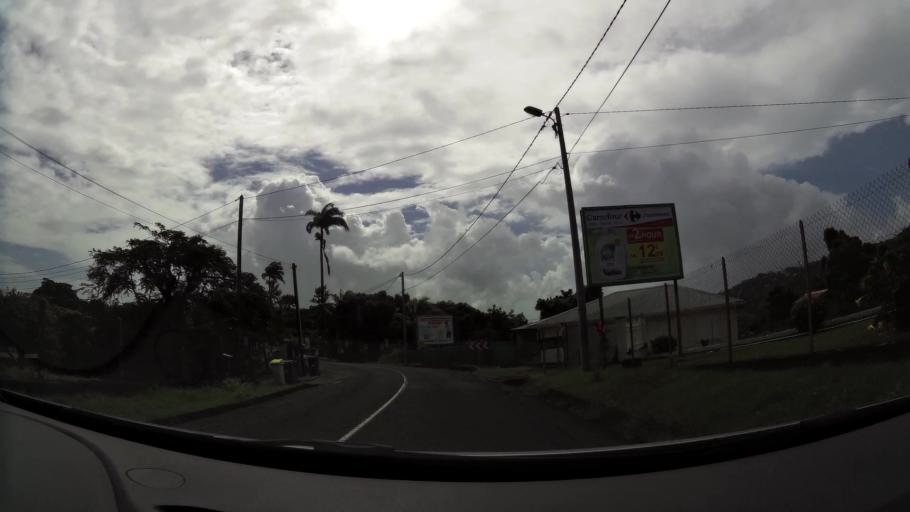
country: MQ
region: Martinique
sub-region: Martinique
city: Saint-Joseph
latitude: 14.6439
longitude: -61.0440
